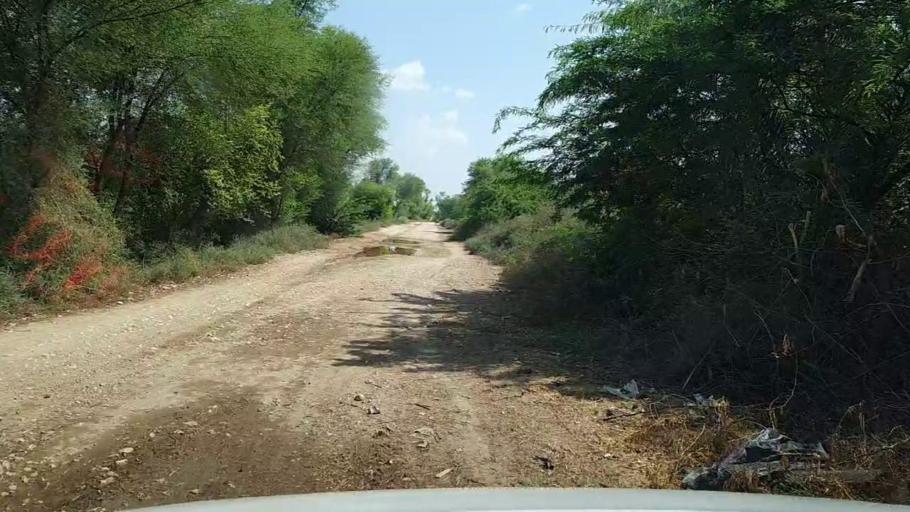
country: PK
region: Sindh
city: Kandiaro
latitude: 27.0075
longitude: 68.3069
